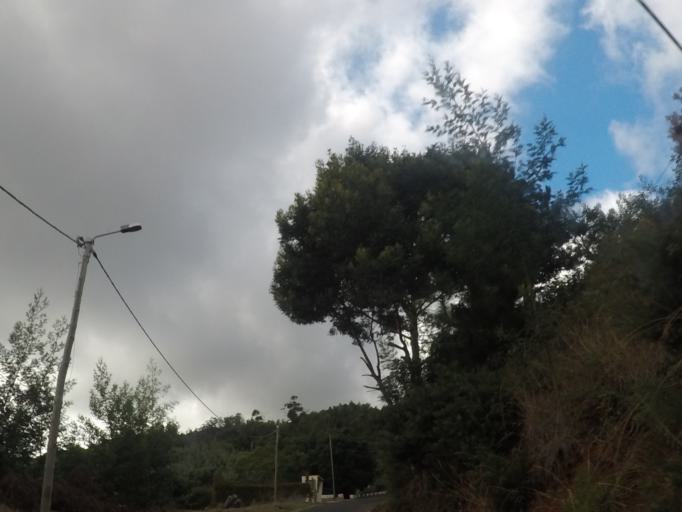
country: PT
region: Madeira
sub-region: Santa Cruz
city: Camacha
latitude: 32.6647
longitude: -16.8292
